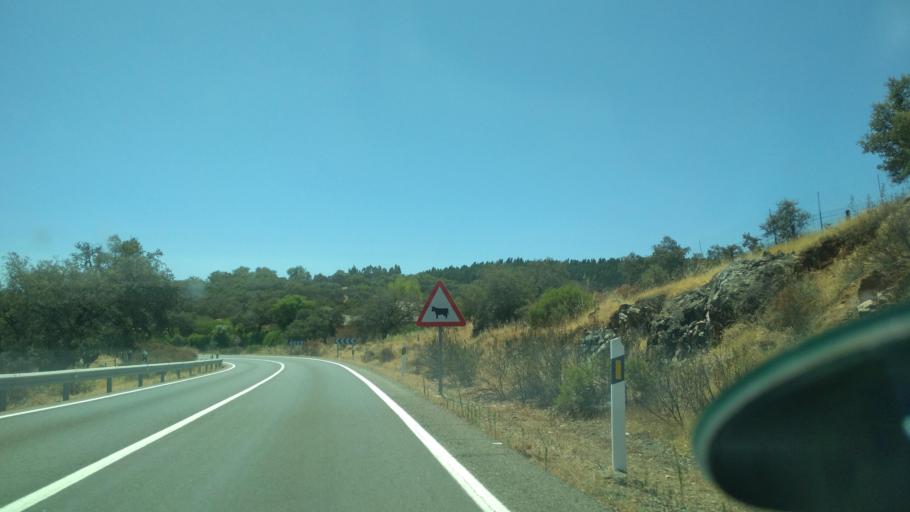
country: ES
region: Andalusia
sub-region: Provincia de Huelva
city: Campofrio
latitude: 37.8258
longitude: -6.5571
